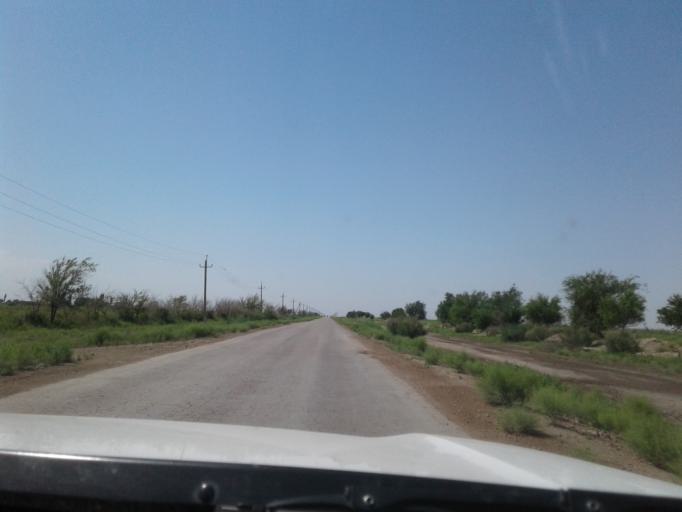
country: TM
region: Dasoguz
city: Koeneuergench
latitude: 41.8534
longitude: 58.7052
